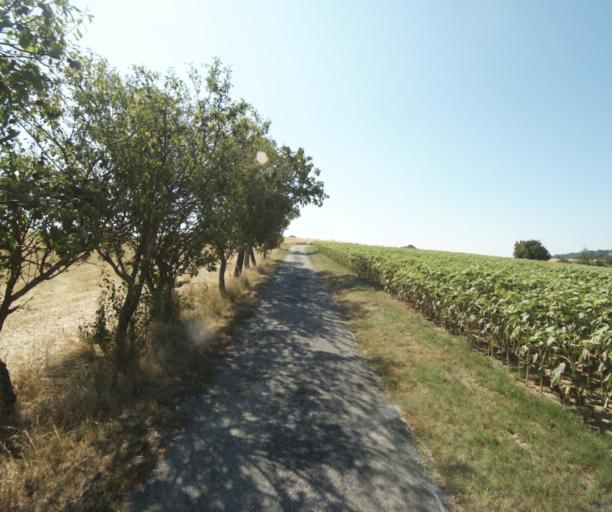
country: FR
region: Midi-Pyrenees
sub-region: Departement de la Haute-Garonne
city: Saint-Felix-Lauragais
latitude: 43.5176
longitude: 1.9396
